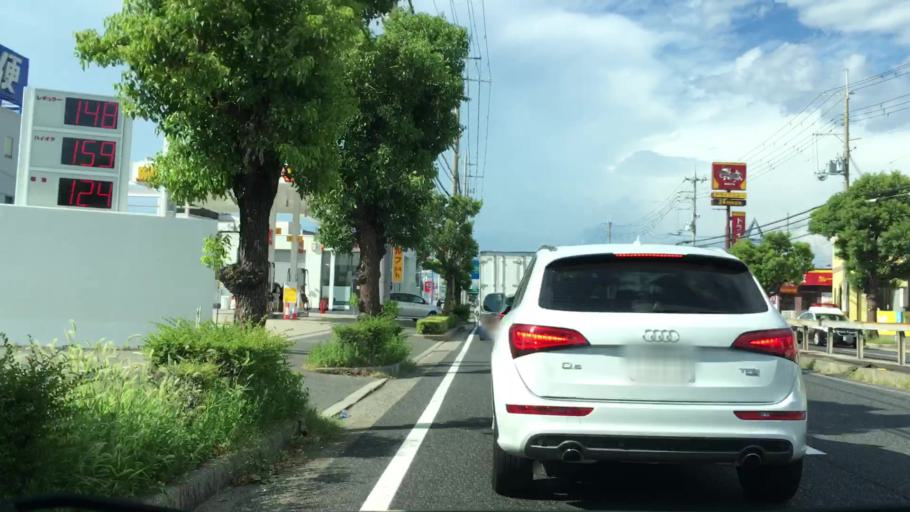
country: JP
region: Hyogo
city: Akashi
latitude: 34.6812
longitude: 134.9822
